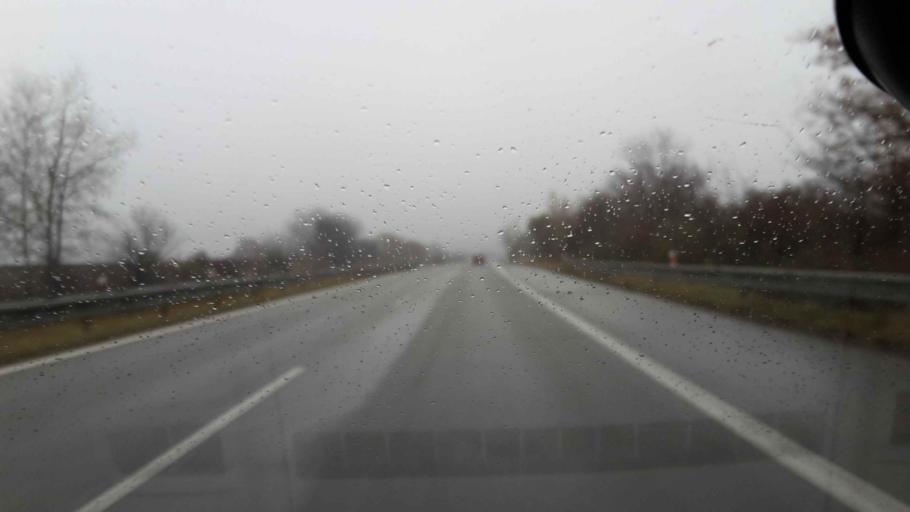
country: CZ
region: South Moravian
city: Podoli
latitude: 49.1839
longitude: 16.7032
